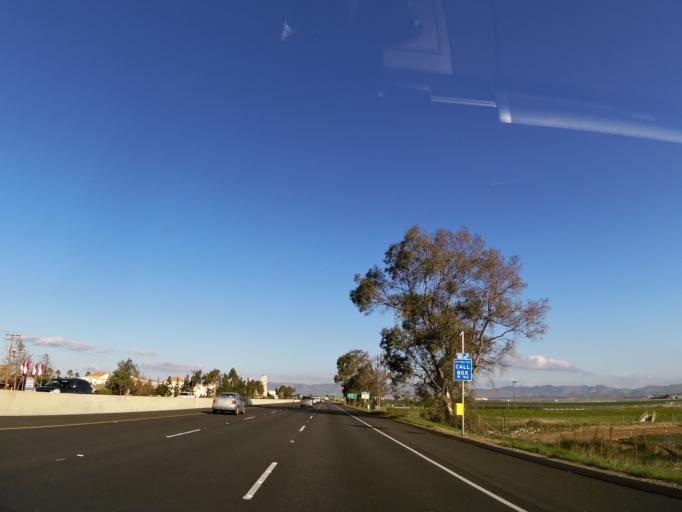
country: US
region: California
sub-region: Santa Barbara County
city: Santa Maria
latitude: 34.9148
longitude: -120.4179
